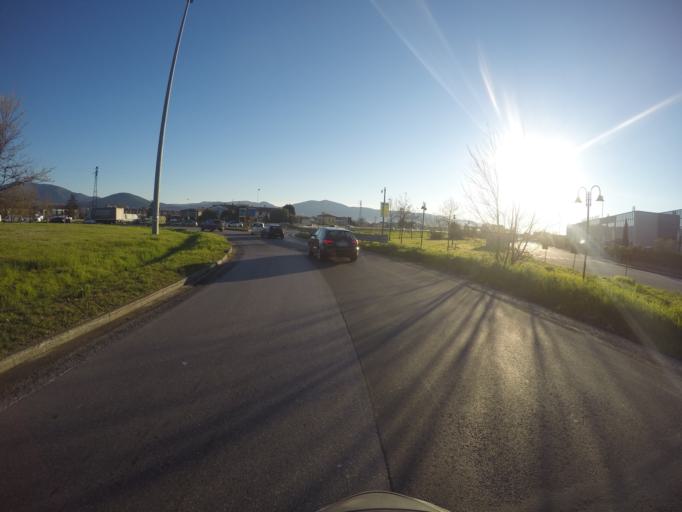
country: IT
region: Tuscany
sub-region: Provincia di Prato
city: Fornacelle
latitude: 43.8833
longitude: 11.0407
